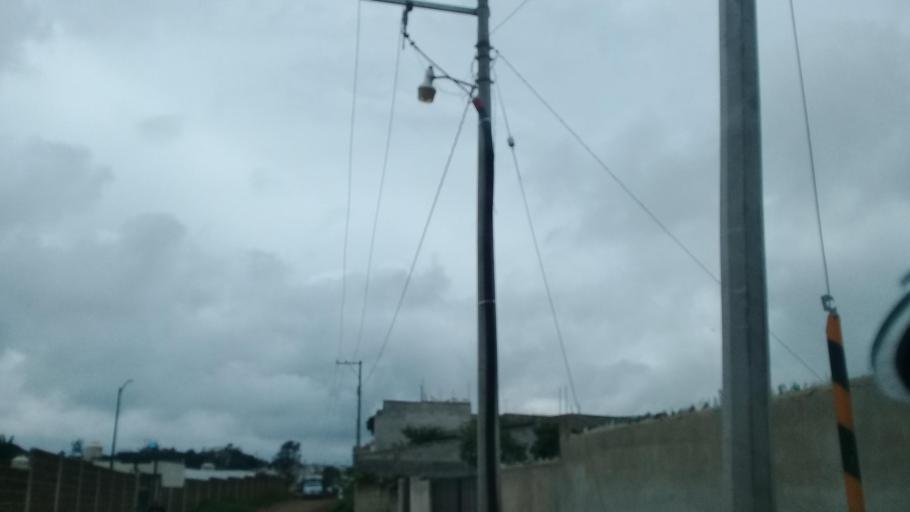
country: MX
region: Veracruz
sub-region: Emiliano Zapata
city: Las Trancas
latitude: 19.4977
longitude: -96.8681
